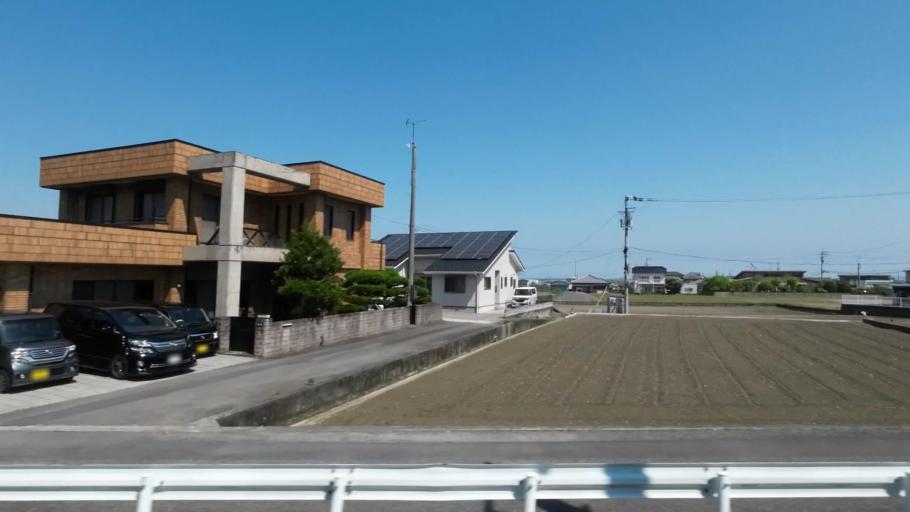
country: JP
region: Ehime
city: Kawanoecho
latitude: 33.9666
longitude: 133.4556
